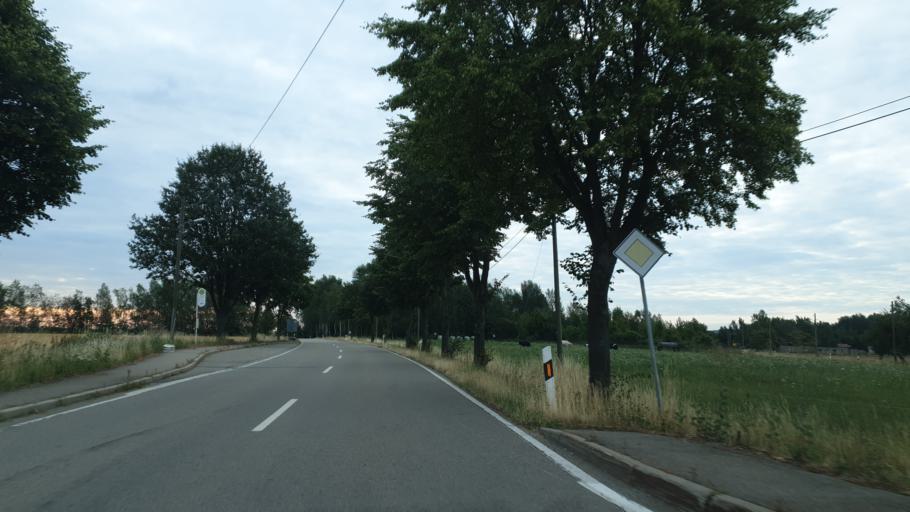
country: DE
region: Saxony
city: Callenberg
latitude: 50.8495
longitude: 12.6422
